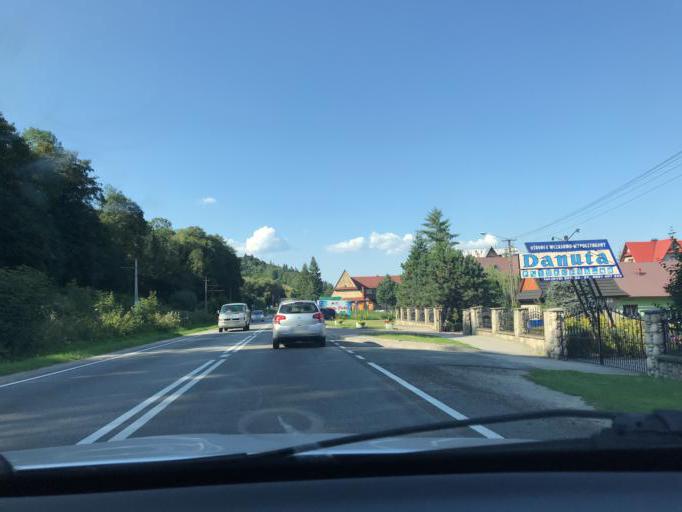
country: PL
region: Lesser Poland Voivodeship
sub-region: Powiat tatrzanski
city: Bialy Dunajec
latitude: 49.3658
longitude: 20.0020
